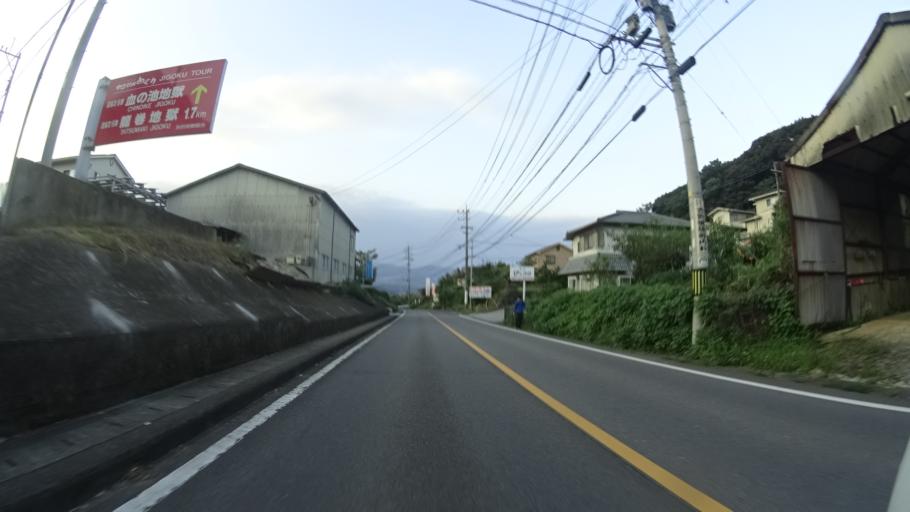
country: JP
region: Oita
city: Beppu
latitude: 33.3189
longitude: 131.4808
